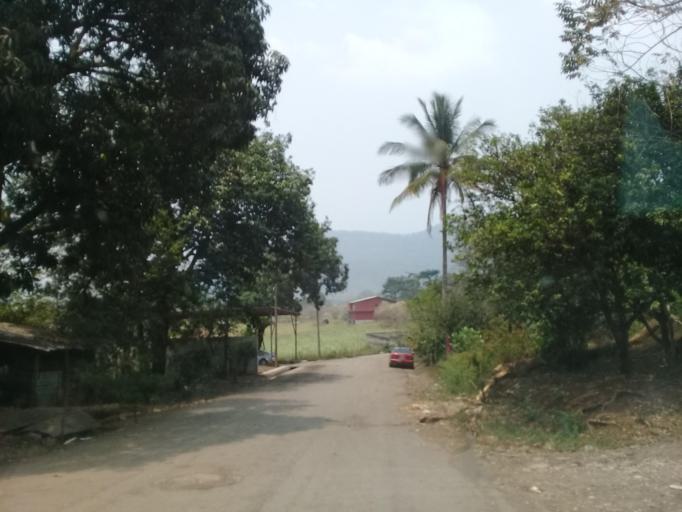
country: MX
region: Veracruz
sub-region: Tezonapa
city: Laguna Chica (Pueblo Nuevo)
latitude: 18.5473
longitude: -96.7315
